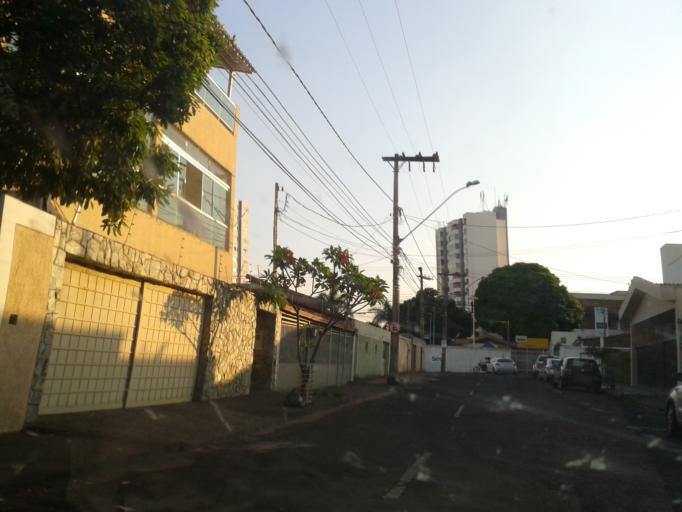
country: BR
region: Minas Gerais
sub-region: Uberlandia
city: Uberlandia
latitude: -18.9107
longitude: -48.2653
